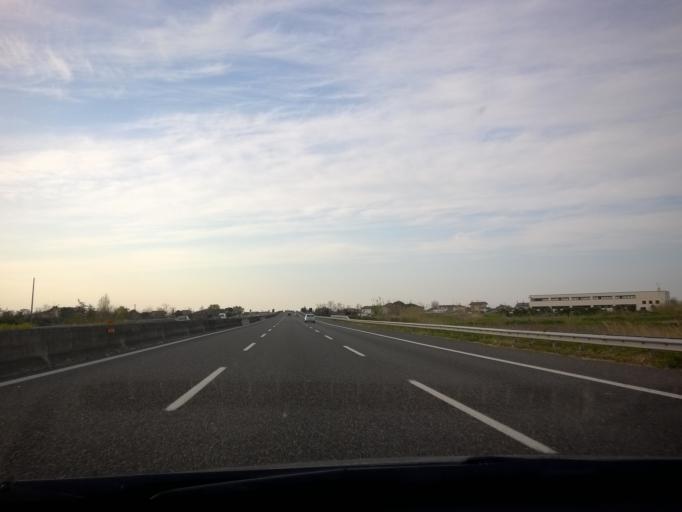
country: IT
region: Emilia-Romagna
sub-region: Forli-Cesena
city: Gatteo-Sant'Angelo
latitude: 44.1259
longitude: 12.3818
